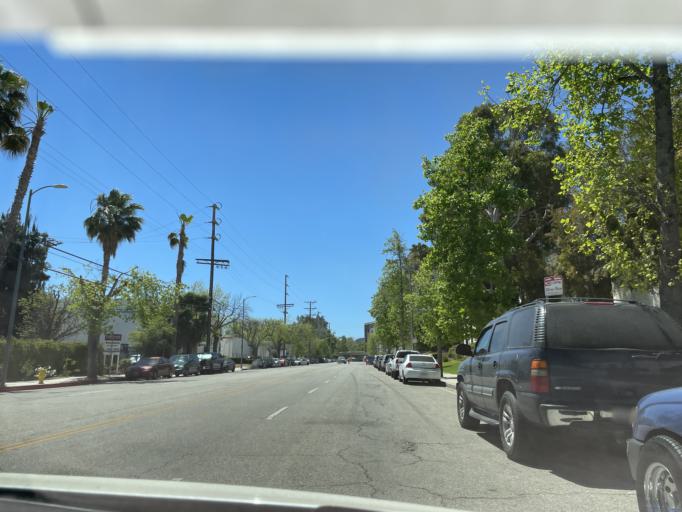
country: US
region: California
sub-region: Los Angeles County
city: Woodland Hills
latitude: 34.1819
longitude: -118.5928
